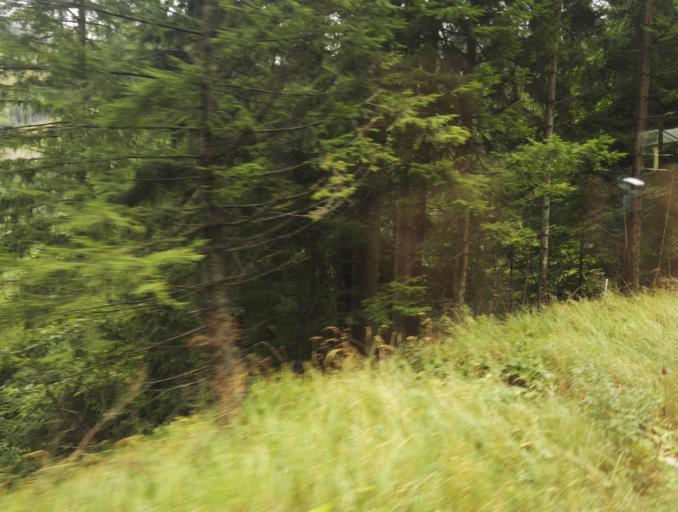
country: AT
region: Styria
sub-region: Politischer Bezirk Leoben
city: Eisenerz
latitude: 47.5279
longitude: 14.9363
